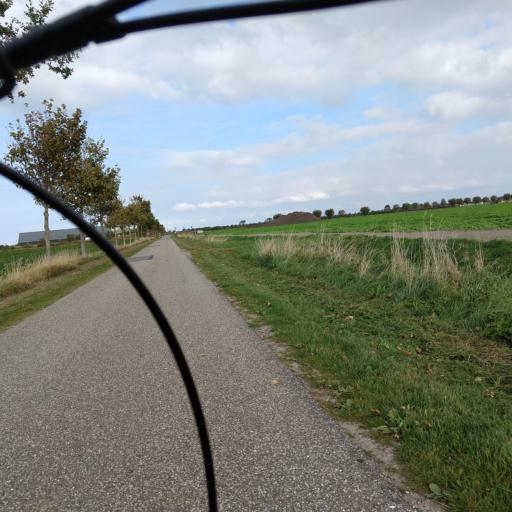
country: NL
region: Zeeland
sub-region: Schouwen-Duiveland
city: Scharendijke
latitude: 51.7072
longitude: 3.9321
